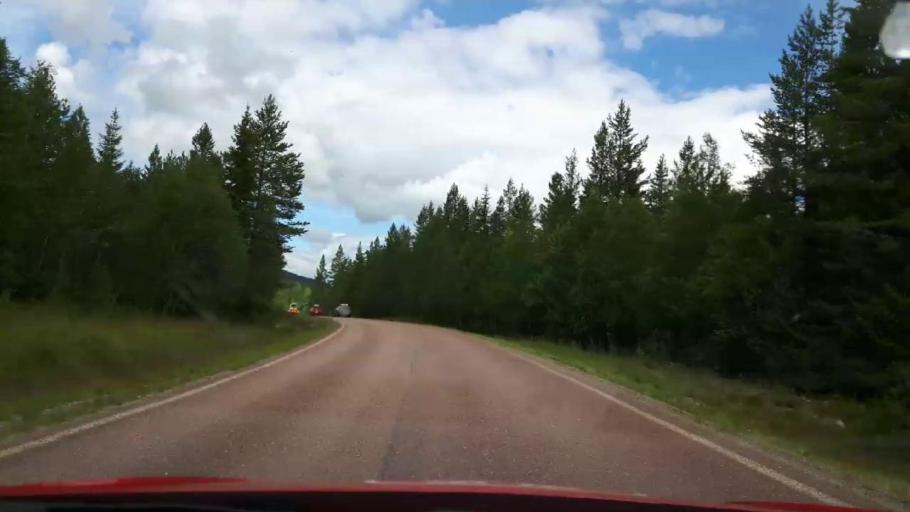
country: NO
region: Hedmark
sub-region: Trysil
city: Innbygda
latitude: 61.8950
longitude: 12.9877
